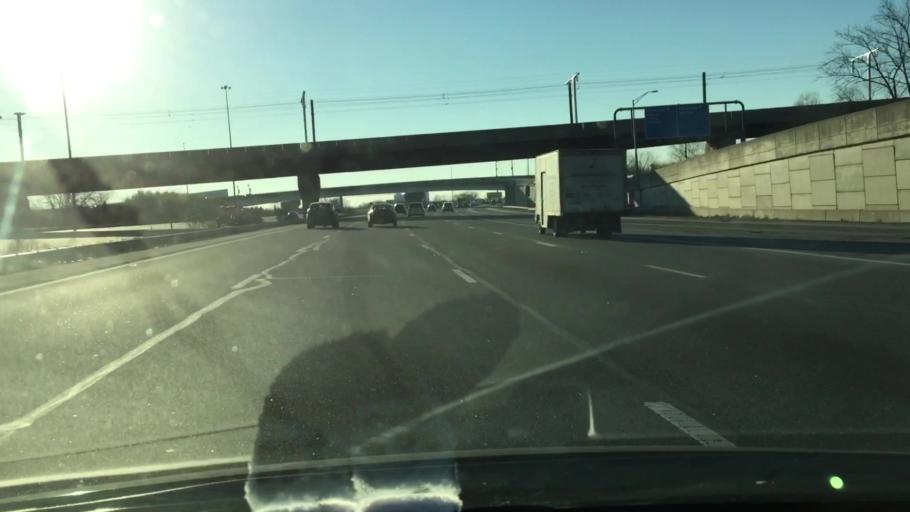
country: US
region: Pennsylvania
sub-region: Delaware County
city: Folcroft
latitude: 39.8772
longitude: -75.2551
